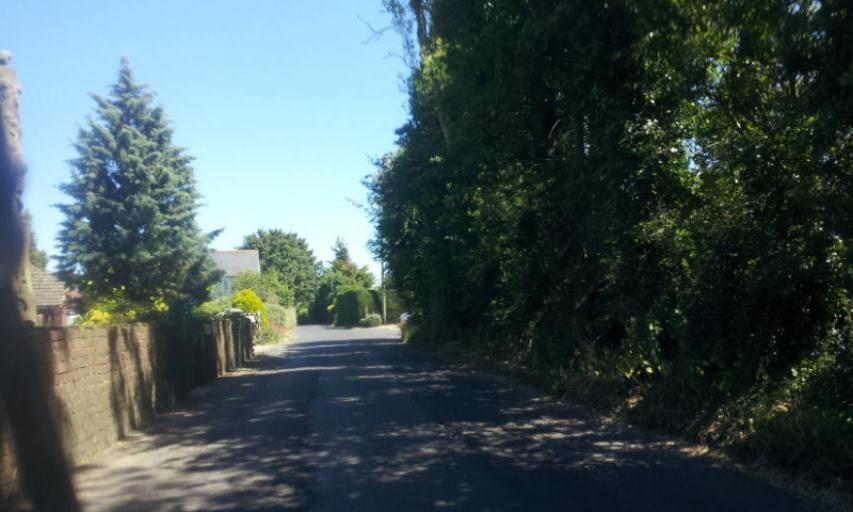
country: GB
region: England
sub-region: Kent
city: Sittingbourne
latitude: 51.3095
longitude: 0.7001
